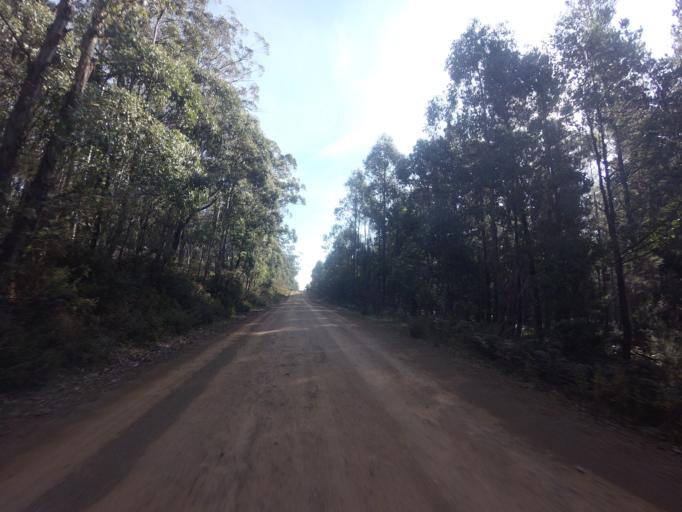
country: AU
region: Tasmania
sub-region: Sorell
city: Sorell
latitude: -42.4891
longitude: 147.5109
